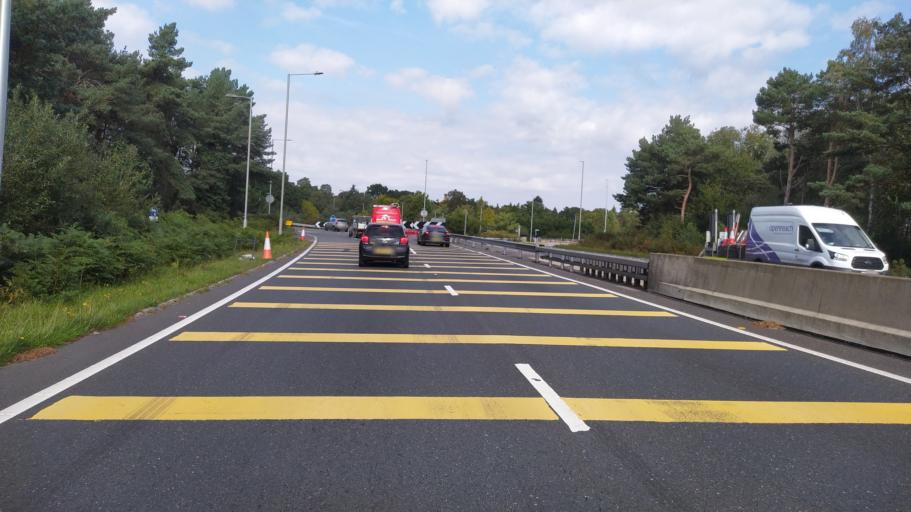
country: GB
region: England
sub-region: Hampshire
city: Ringwood
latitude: 50.8376
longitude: -1.8120
